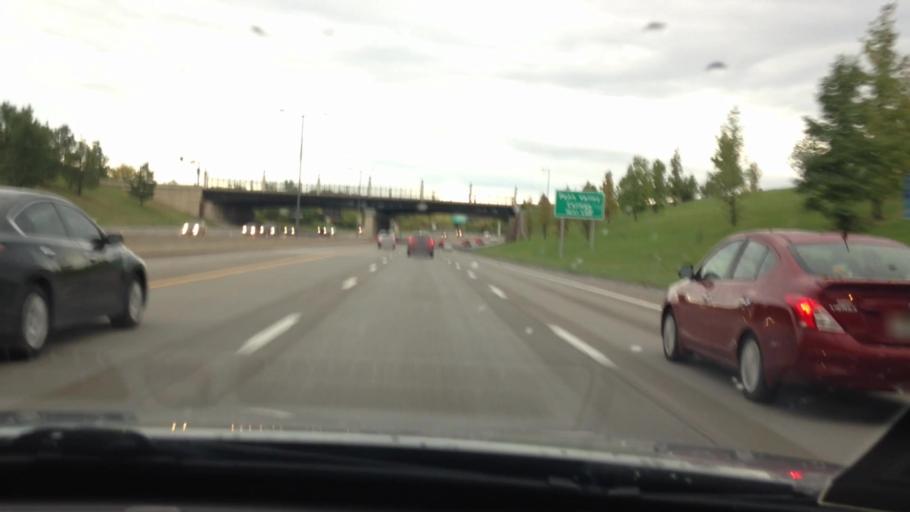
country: US
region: Missouri
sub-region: Jackson County
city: Kansas City
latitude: 39.0843
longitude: -94.5684
